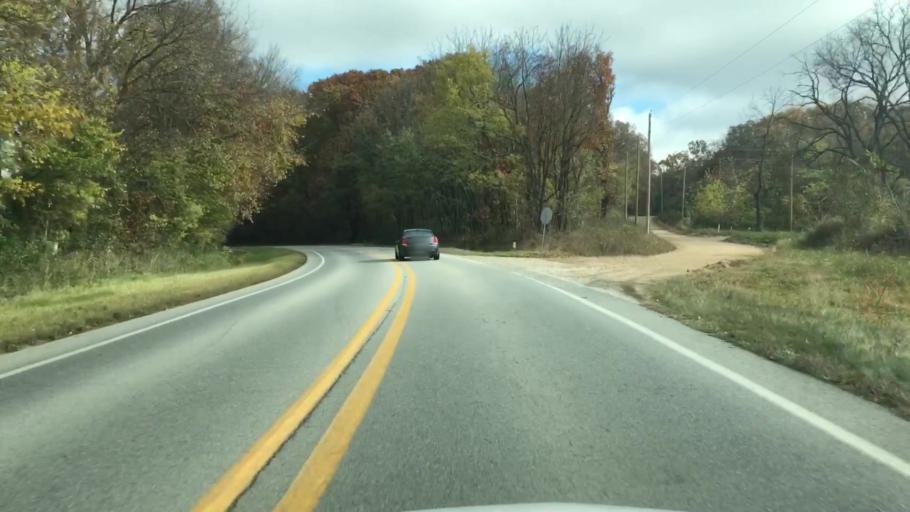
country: US
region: Arkansas
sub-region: Benton County
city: Gentry
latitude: 36.2559
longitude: -94.4318
